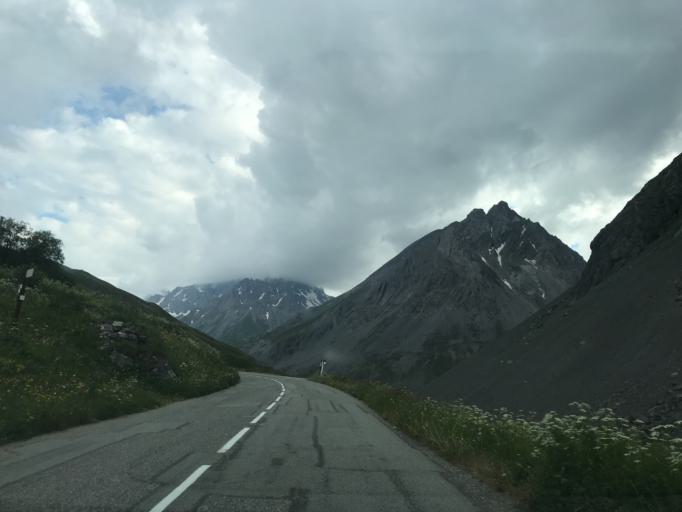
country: FR
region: Rhone-Alpes
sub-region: Departement de la Savoie
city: Valloire
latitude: 45.1138
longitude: 6.4236
